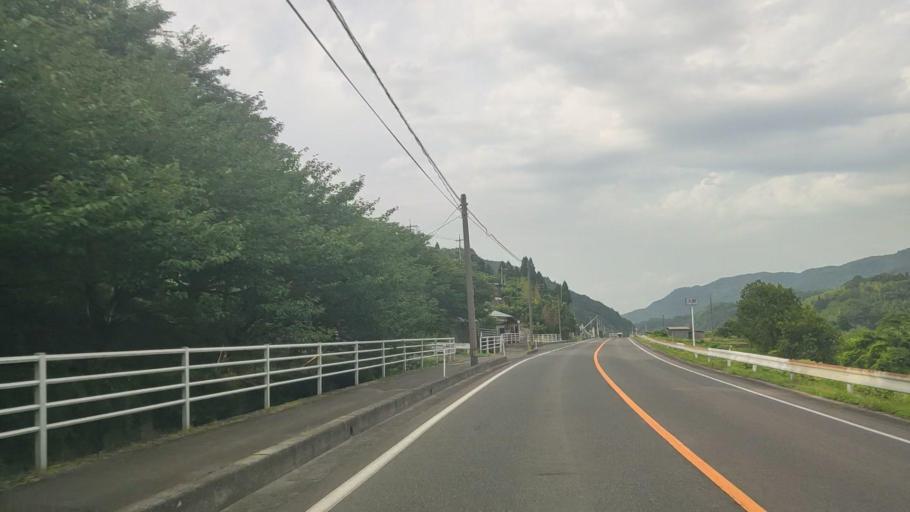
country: JP
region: Tottori
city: Kurayoshi
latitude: 35.3455
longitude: 133.8409
